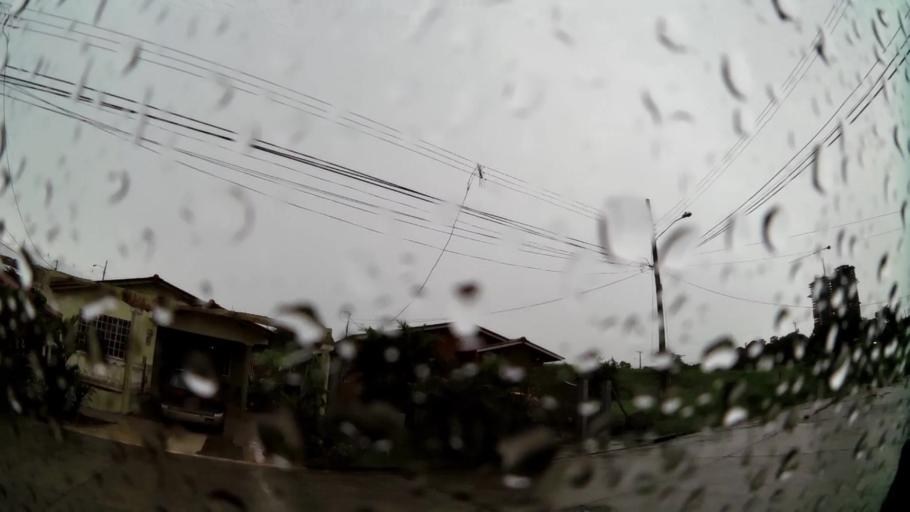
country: PA
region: Panama
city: San Miguelito
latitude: 9.0553
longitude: -79.4745
